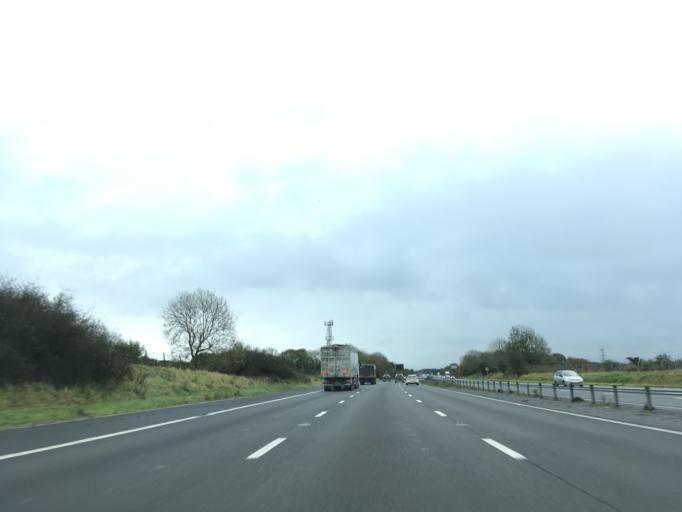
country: GB
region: England
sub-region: Wiltshire
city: Nettleton
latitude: 51.5187
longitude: -2.2590
